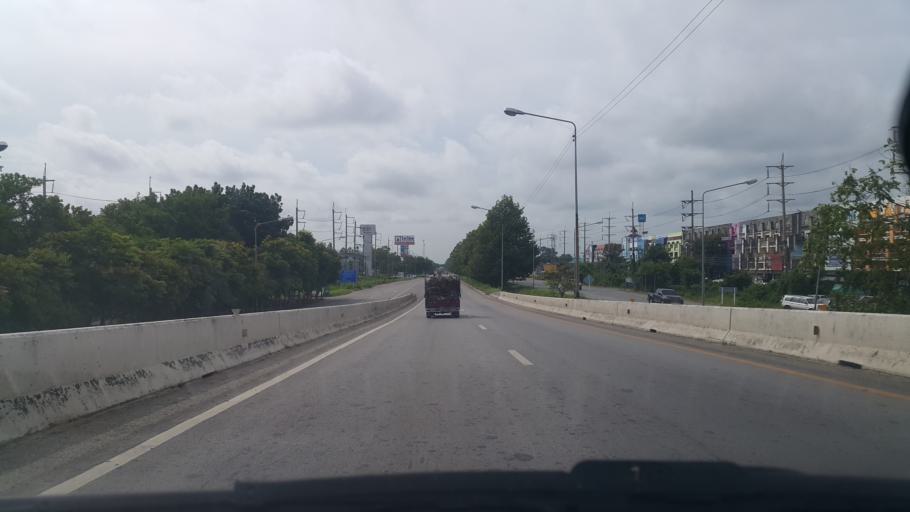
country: TH
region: Rayong
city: Rayong
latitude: 12.6642
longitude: 101.3088
